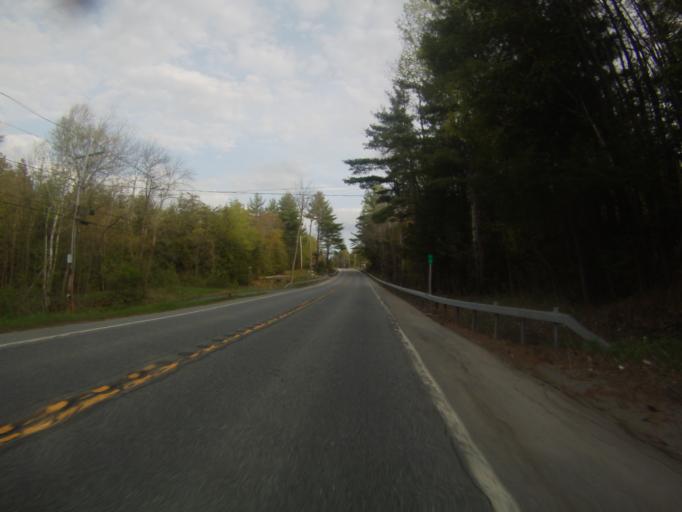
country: US
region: New York
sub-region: Warren County
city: Warrensburg
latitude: 43.6651
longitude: -73.9584
